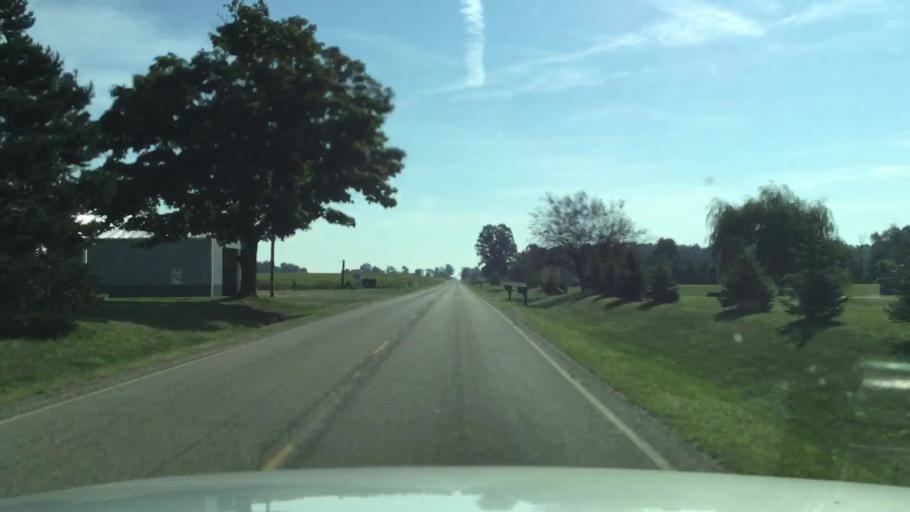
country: US
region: Michigan
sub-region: Lenawee County
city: Hudson
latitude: 41.9276
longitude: -84.4002
